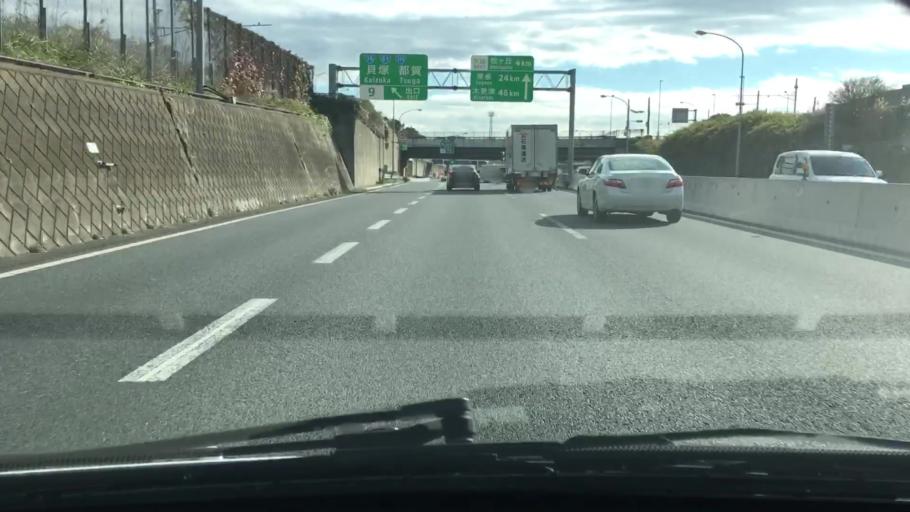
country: JP
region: Chiba
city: Chiba
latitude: 35.6257
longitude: 140.1393
